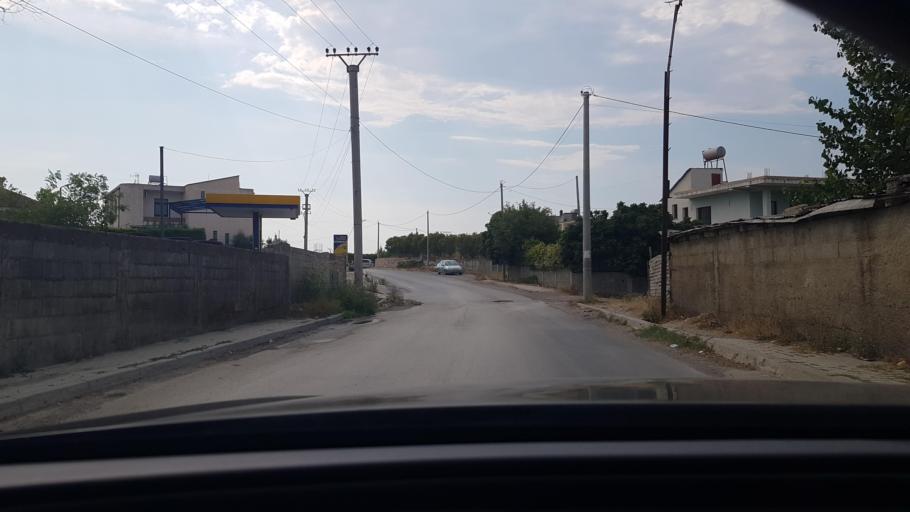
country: AL
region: Durres
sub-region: Rrethi i Durresit
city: Katundi i Ri
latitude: 41.4271
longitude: 19.5471
